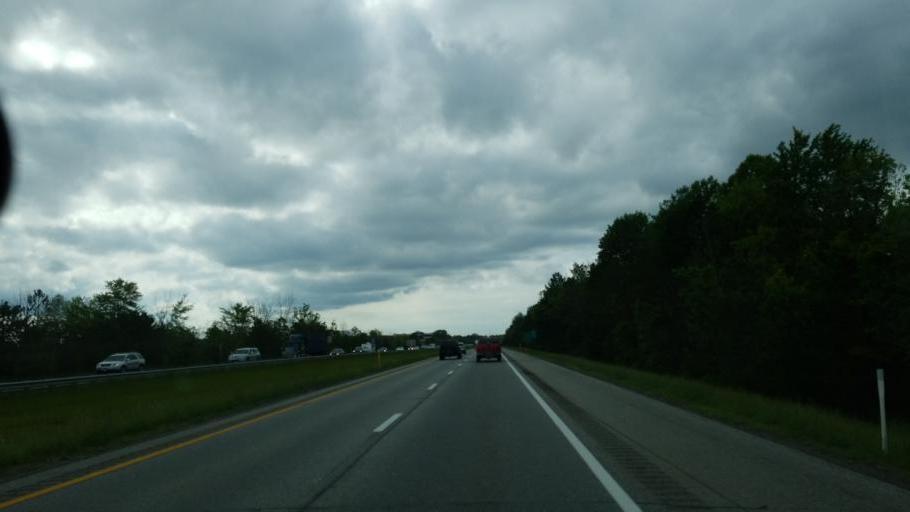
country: US
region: Ohio
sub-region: Cuyahoga County
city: Solon
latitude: 41.3993
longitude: -81.4552
